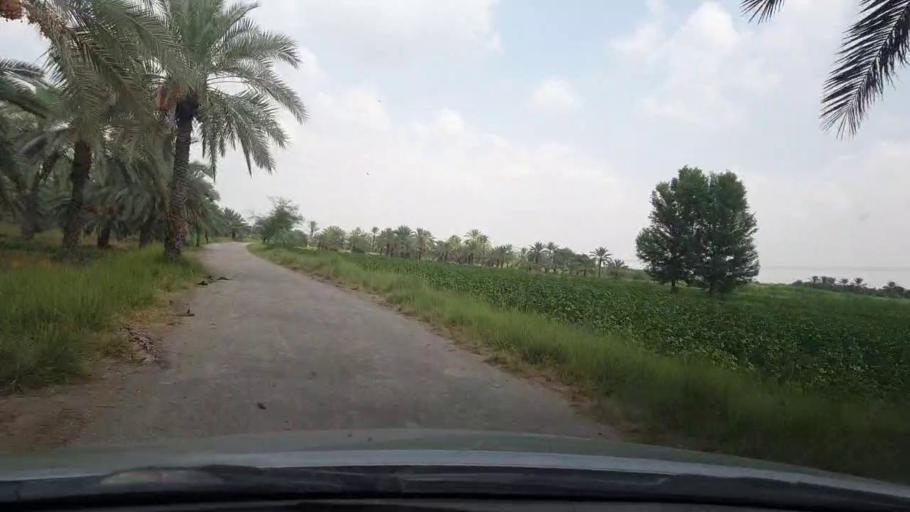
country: PK
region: Sindh
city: Khairpur
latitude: 27.4652
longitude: 68.7579
